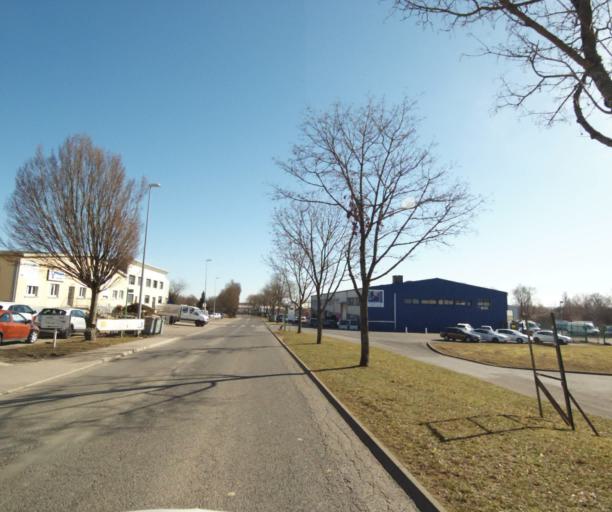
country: FR
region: Lorraine
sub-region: Departement de Meurthe-et-Moselle
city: Fleville-devant-Nancy
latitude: 48.6179
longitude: 6.1870
